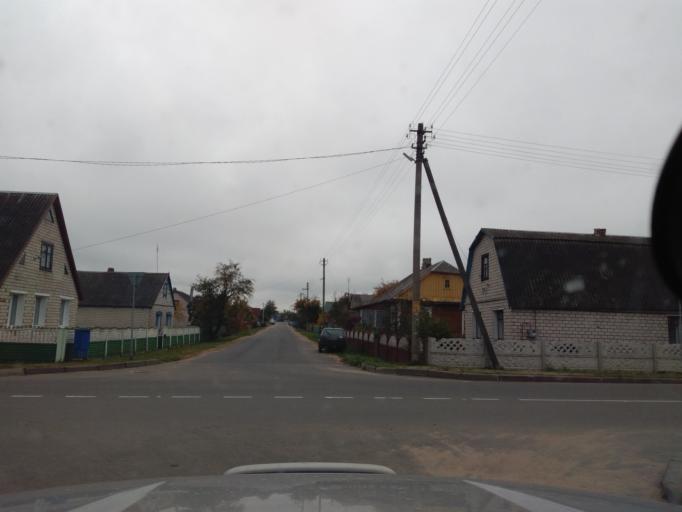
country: BY
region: Minsk
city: Kapyl'
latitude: 53.1430
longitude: 27.0948
